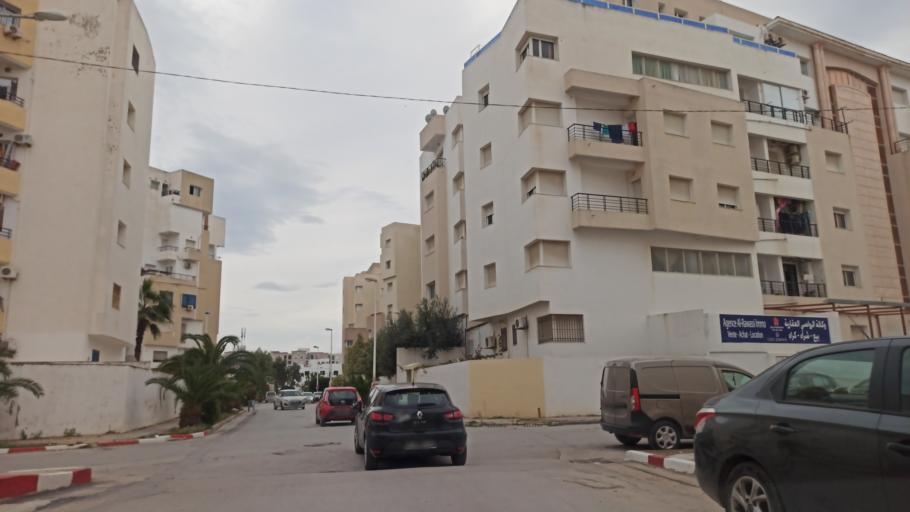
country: TN
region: Tunis
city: La Goulette
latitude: 36.8601
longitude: 10.2646
